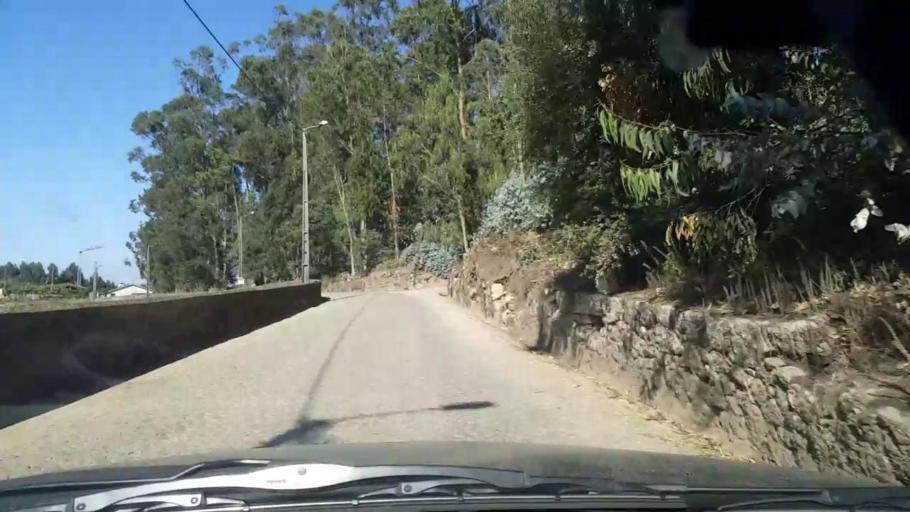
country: PT
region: Braga
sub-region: Vila Nova de Famalicao
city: Ribeirao
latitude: 41.3772
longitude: -8.6379
